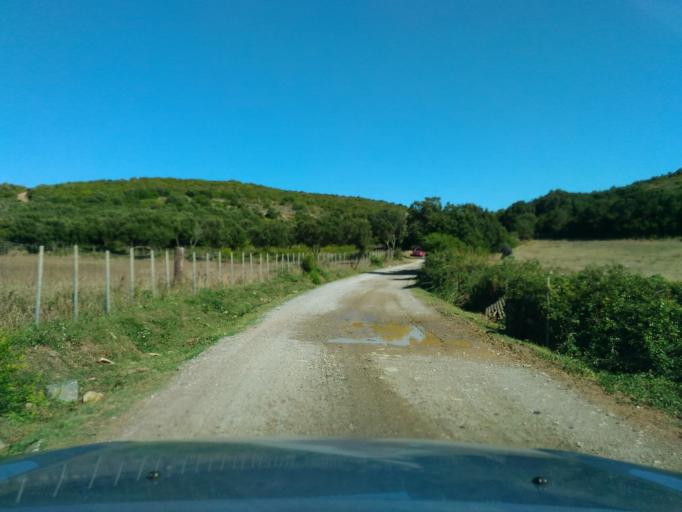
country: FR
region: Corsica
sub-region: Departement de la Haute-Corse
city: Brando
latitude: 42.9692
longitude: 9.4521
